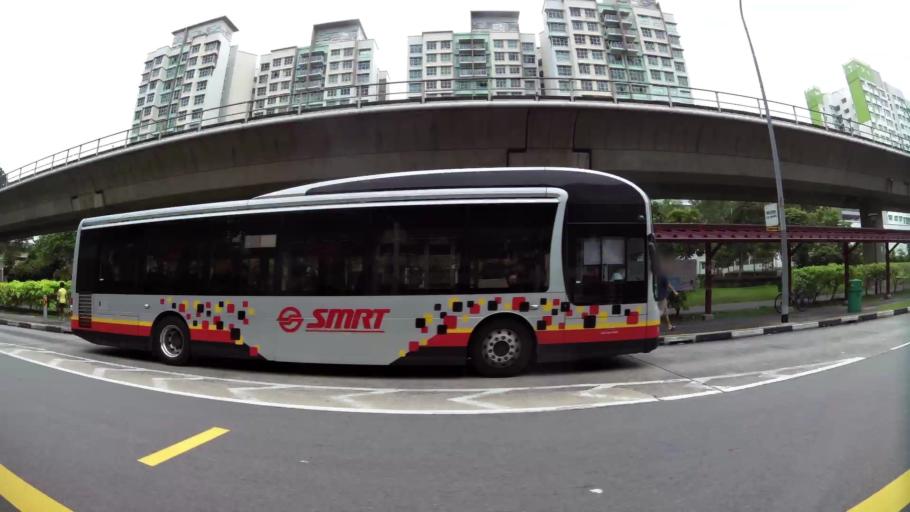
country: MY
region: Johor
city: Johor Bahru
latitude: 1.4390
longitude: 103.7941
